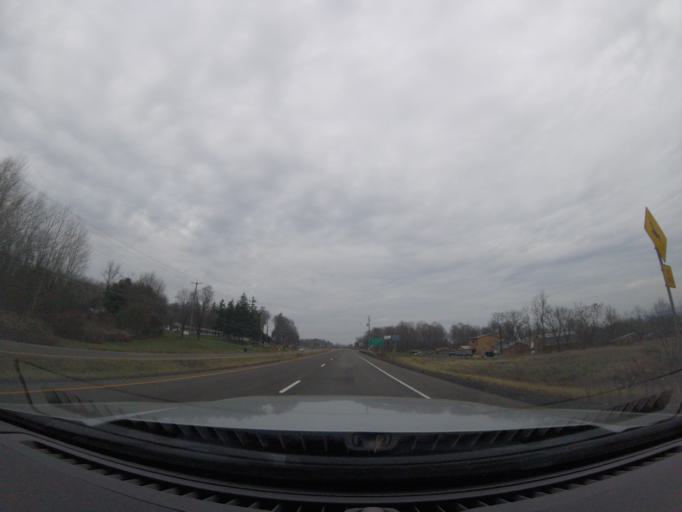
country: US
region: New York
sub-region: Schuyler County
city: Watkins Glen
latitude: 42.4168
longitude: -76.9020
